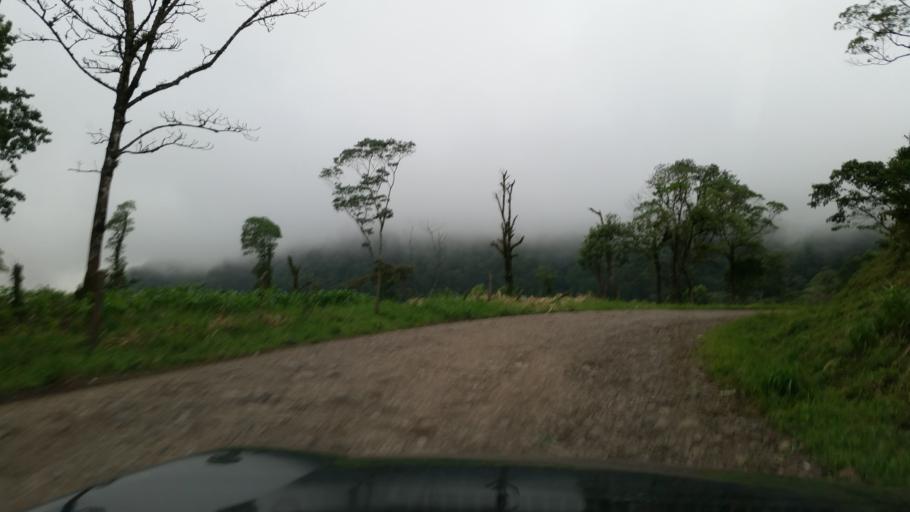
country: NI
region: Jinotega
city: San Jose de Bocay
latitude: 13.2823
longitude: -85.7189
